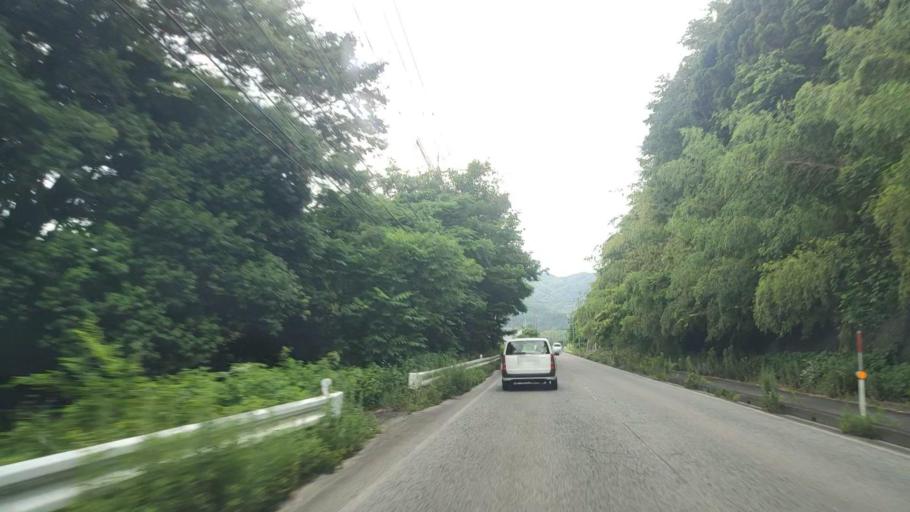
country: JP
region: Tottori
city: Yonago
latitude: 35.3392
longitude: 133.4341
